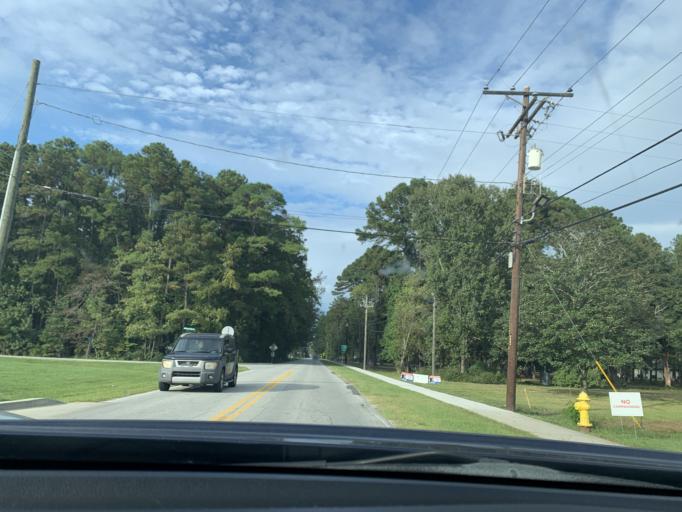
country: US
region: Georgia
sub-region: Chatham County
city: Pooler
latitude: 32.1073
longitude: -81.2519
